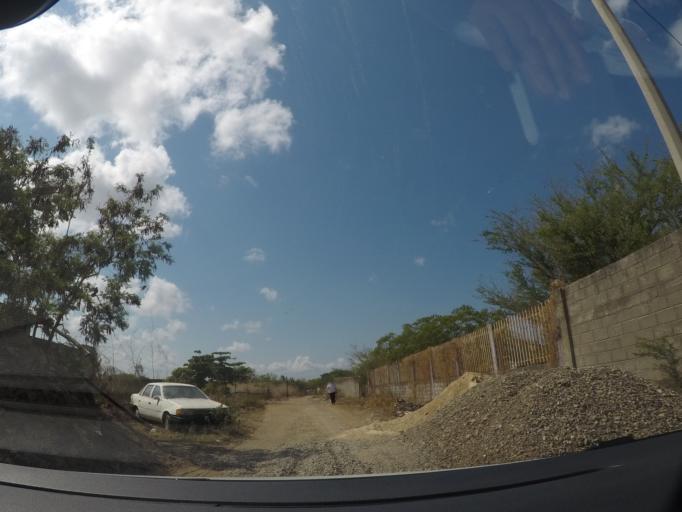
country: MX
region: Oaxaca
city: Juchitan de Zaragoza
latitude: 16.4373
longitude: -95.0087
